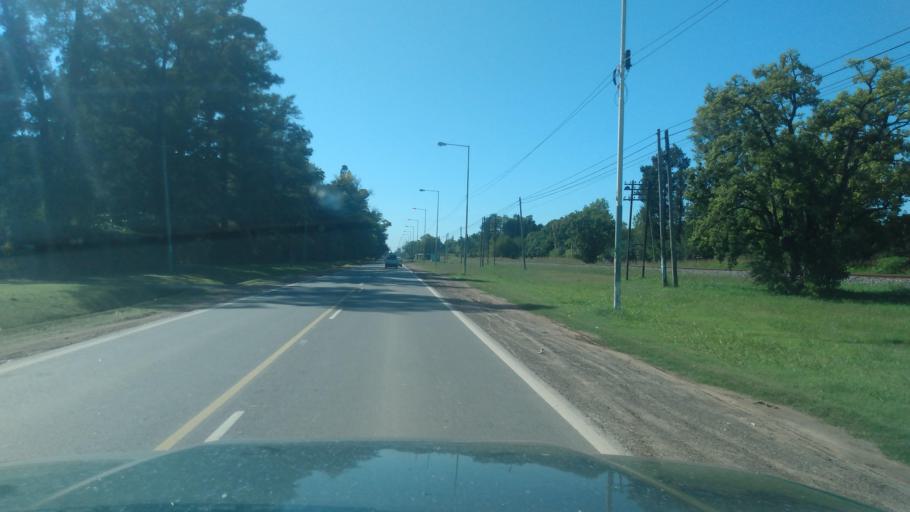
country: AR
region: Buenos Aires
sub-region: Partido de General Rodriguez
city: General Rodriguez
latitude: -34.6024
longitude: -58.9797
